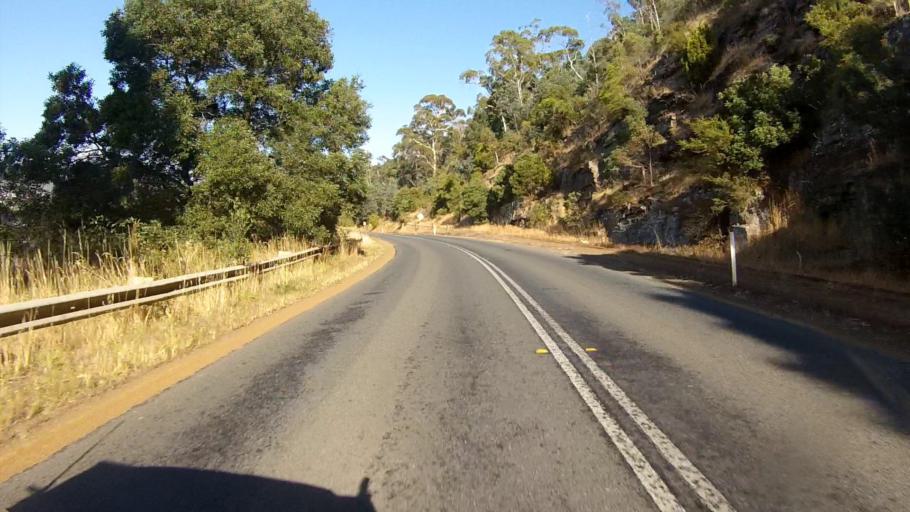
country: AU
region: Tasmania
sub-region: Derwent Valley
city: New Norfolk
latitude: -42.7695
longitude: 147.0716
